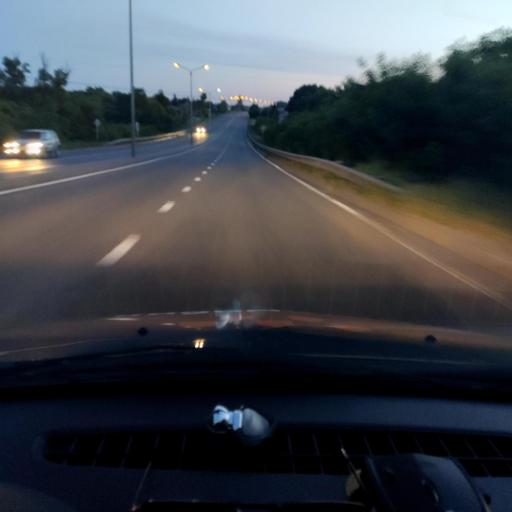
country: RU
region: Belgorod
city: Gubkin
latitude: 51.2754
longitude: 37.5893
